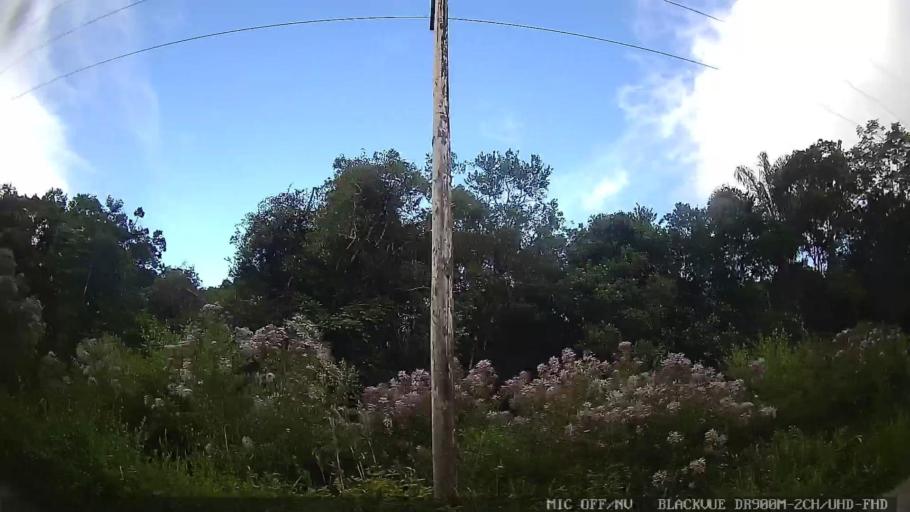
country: BR
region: Sao Paulo
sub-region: Itanhaem
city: Itanhaem
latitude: -24.1813
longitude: -46.9387
